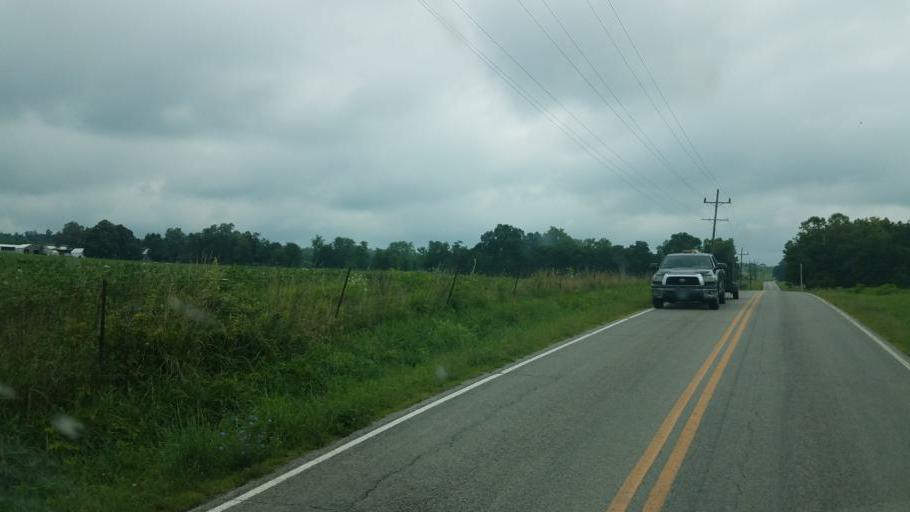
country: US
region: Ohio
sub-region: Highland County
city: Hillsboro
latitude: 39.2217
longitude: -83.5503
